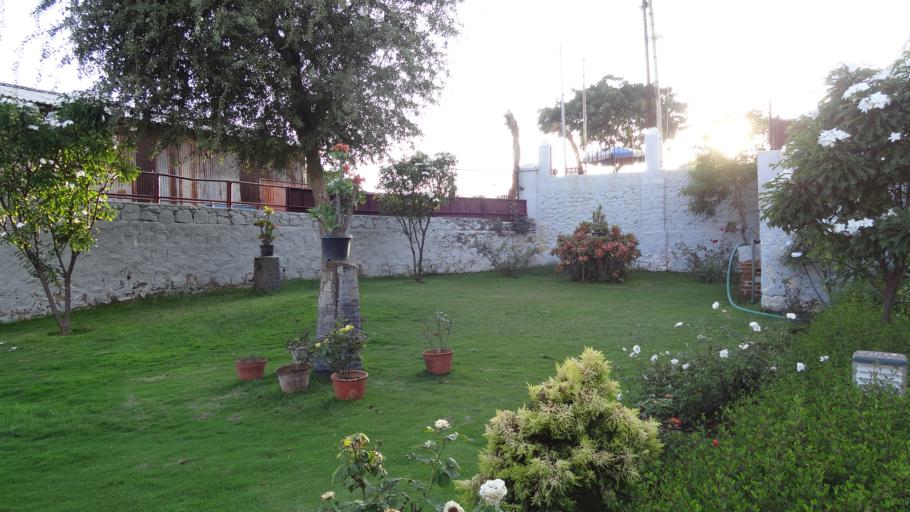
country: IN
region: Tamil Nadu
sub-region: Kanniyakumari
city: Kanniyakumari
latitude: 8.0813
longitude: 77.5500
